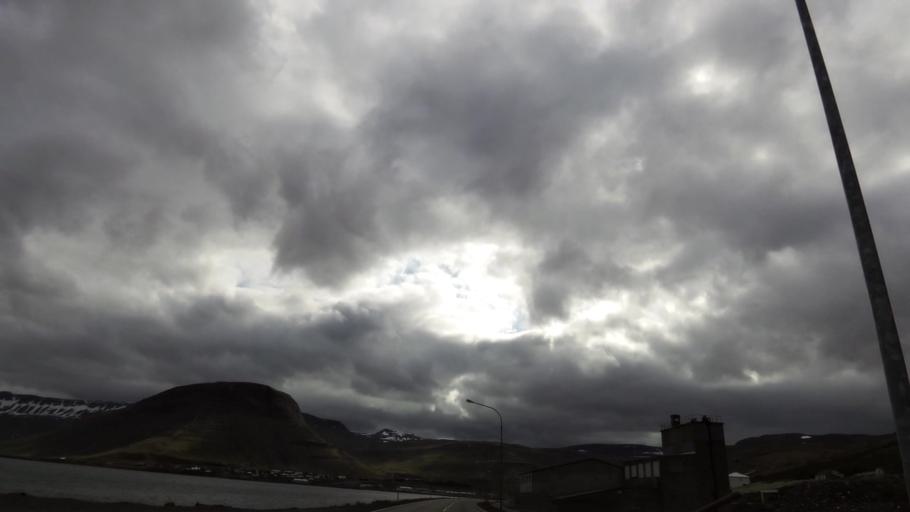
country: IS
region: Westfjords
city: Isafjoerdur
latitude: 66.0687
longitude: -23.1520
